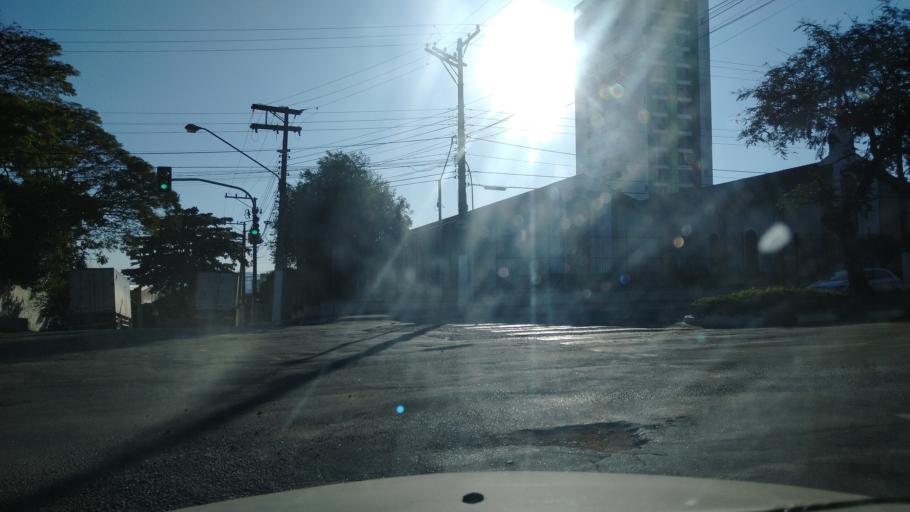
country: BR
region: Sao Paulo
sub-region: Osasco
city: Osasco
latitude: -23.5177
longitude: -46.7805
